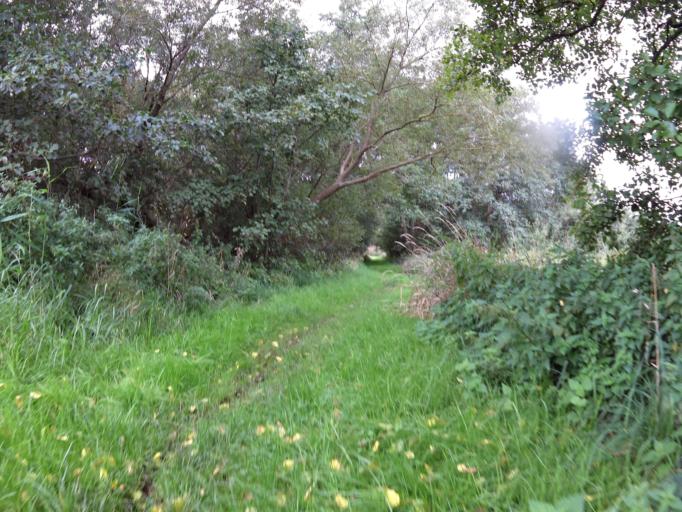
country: DE
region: Schleswig-Holstein
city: Krummbek
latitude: 54.4172
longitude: 10.3968
